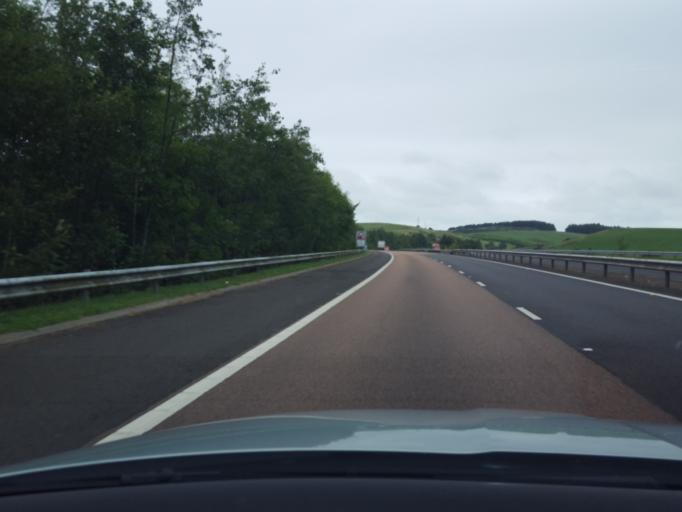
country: GB
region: Scotland
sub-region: Perth and Kinross
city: Bridge of Earn
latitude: 56.3004
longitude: -3.3848
